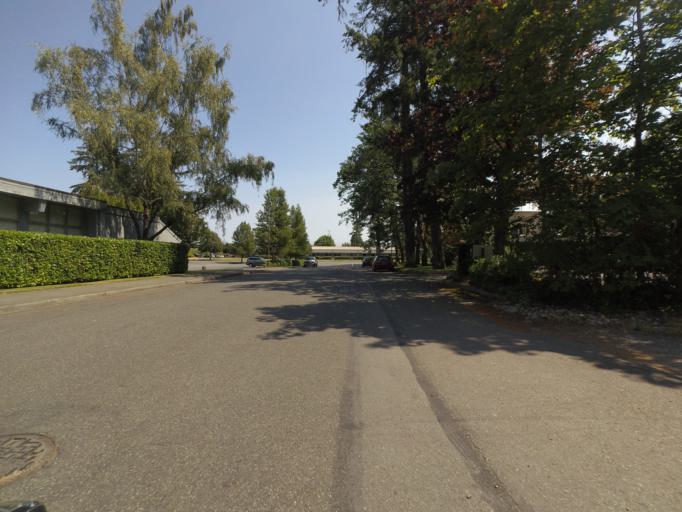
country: US
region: Washington
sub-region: Pierce County
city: Lakewood
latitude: 47.1595
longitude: -122.5218
